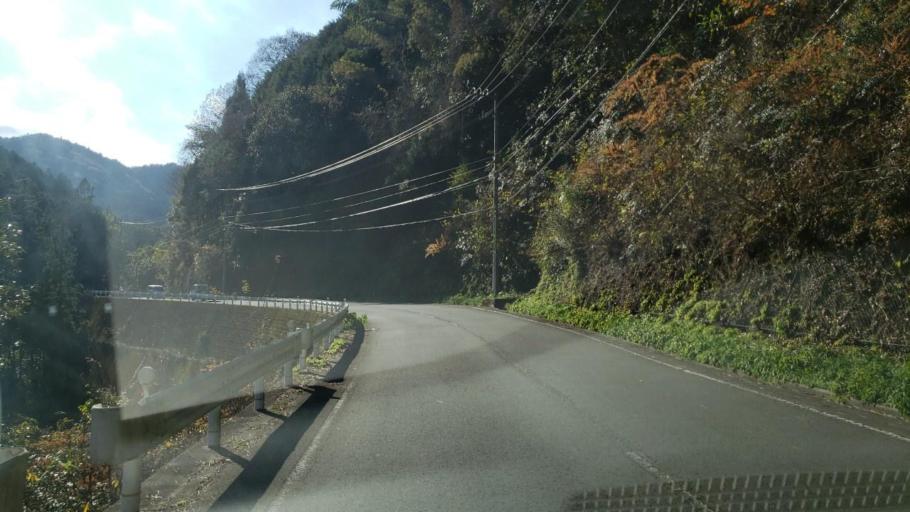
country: JP
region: Tokushima
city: Wakimachi
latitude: 34.0179
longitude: 134.0356
